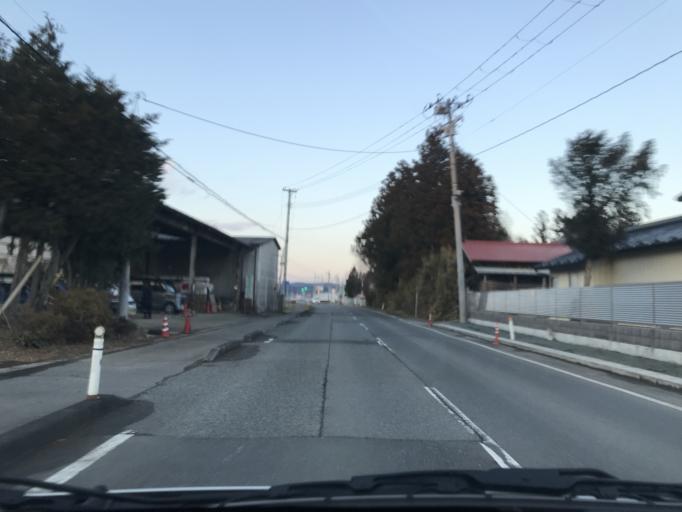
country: JP
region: Iwate
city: Ichinoseki
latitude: 38.7819
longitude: 141.1162
